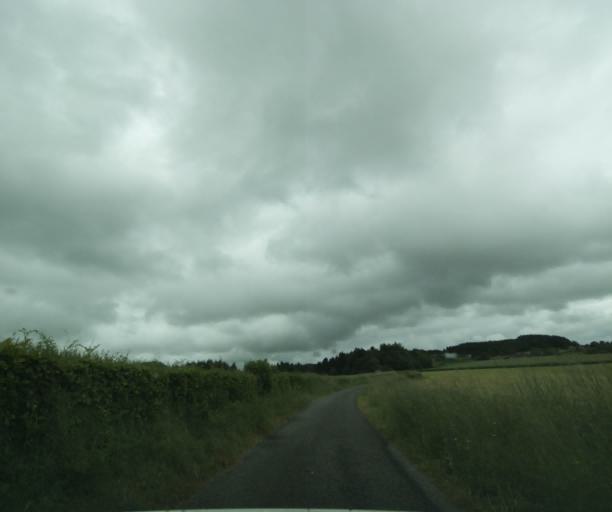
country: FR
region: Bourgogne
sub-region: Departement de Saone-et-Loire
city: Matour
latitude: 46.4418
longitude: 4.4437
